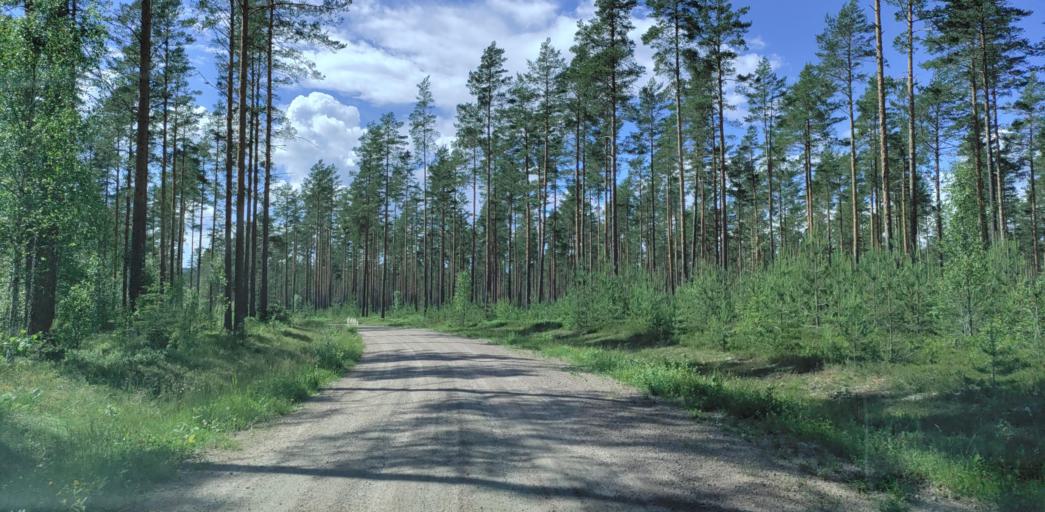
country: SE
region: Vaermland
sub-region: Munkfors Kommun
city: Munkfors
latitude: 59.9612
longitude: 13.5082
